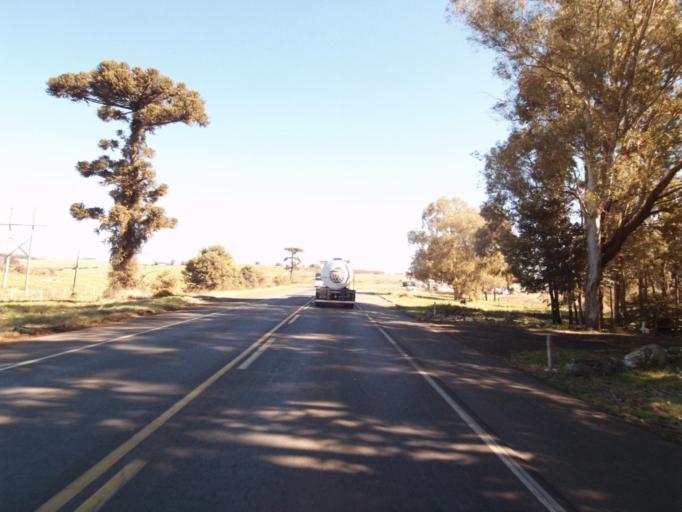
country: BR
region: Santa Catarina
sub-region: Xanxere
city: Xanxere
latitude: -26.8771
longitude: -52.3319
